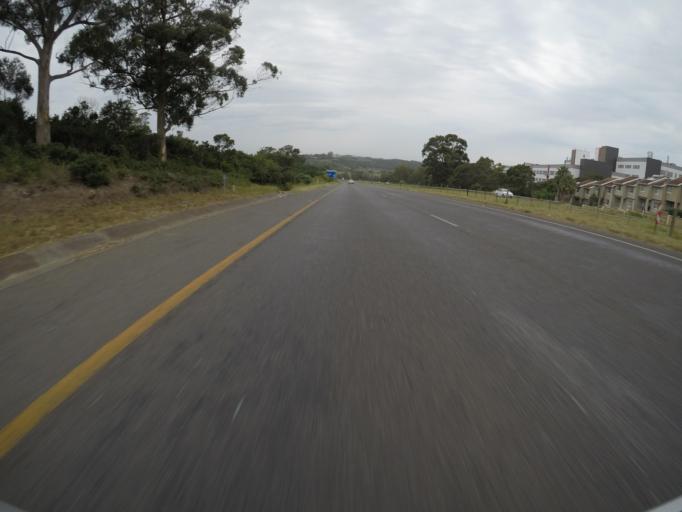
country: ZA
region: Eastern Cape
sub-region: Buffalo City Metropolitan Municipality
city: East London
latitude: -32.9483
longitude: 27.9372
